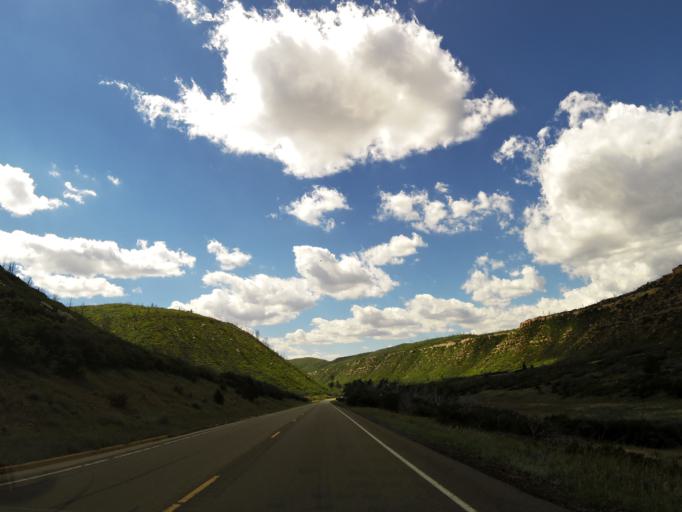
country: US
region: Colorado
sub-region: Montezuma County
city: Mancos
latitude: 37.2911
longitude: -108.4134
